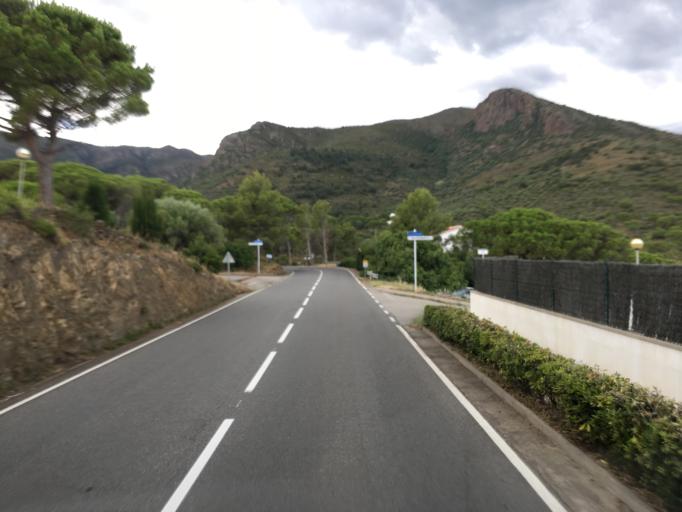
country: ES
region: Catalonia
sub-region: Provincia de Girona
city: Llanca
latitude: 42.3416
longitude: 3.1870
